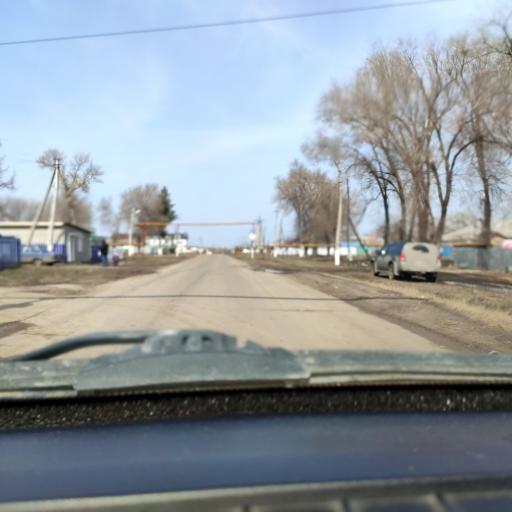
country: RU
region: Samara
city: Smyshlyayevka
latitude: 53.1824
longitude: 50.4614
